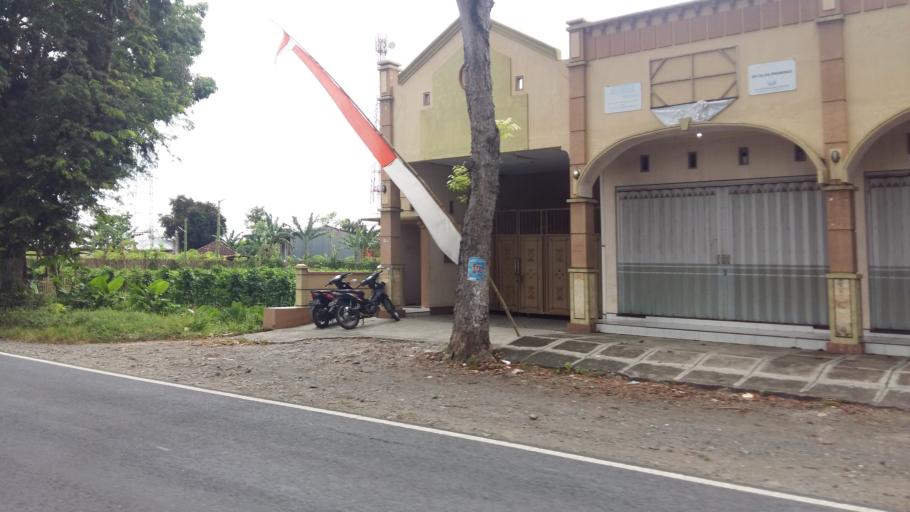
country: ID
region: East Java
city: Krajan
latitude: -8.3285
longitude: 114.2828
